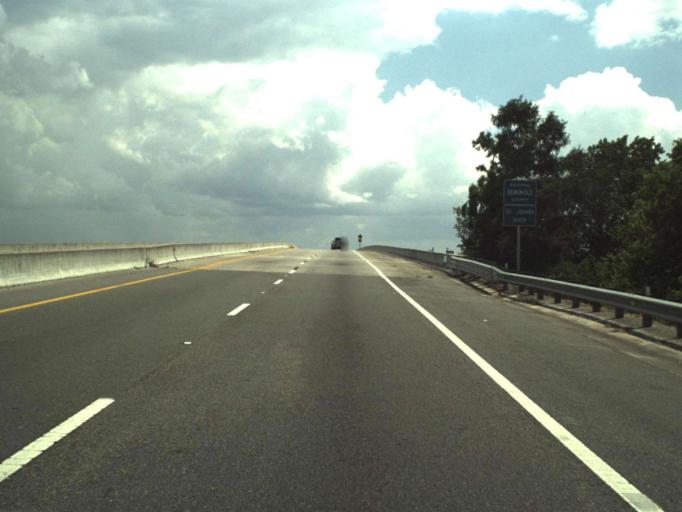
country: US
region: Florida
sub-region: Volusia County
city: DeBary
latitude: 28.8399
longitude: -81.3235
